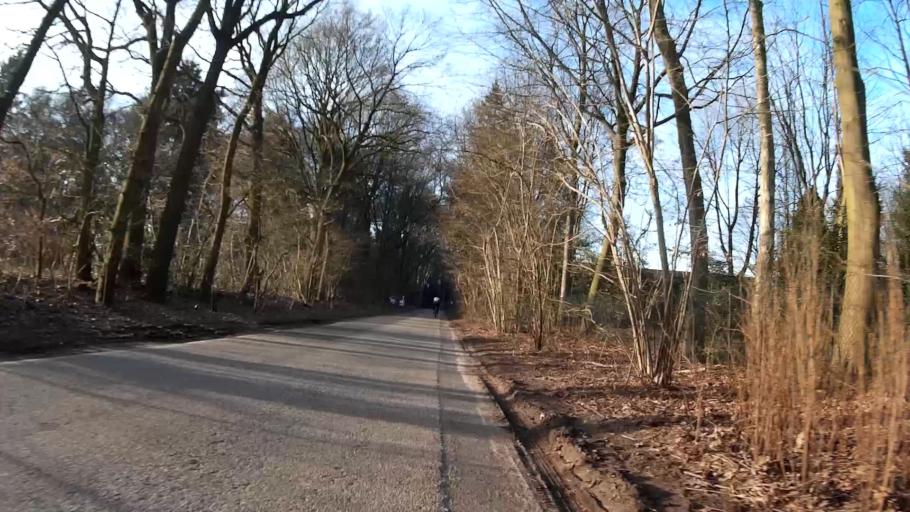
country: NL
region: Utrecht
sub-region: Gemeente Rhenen
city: Rhenen
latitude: 51.9915
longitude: 5.5586
